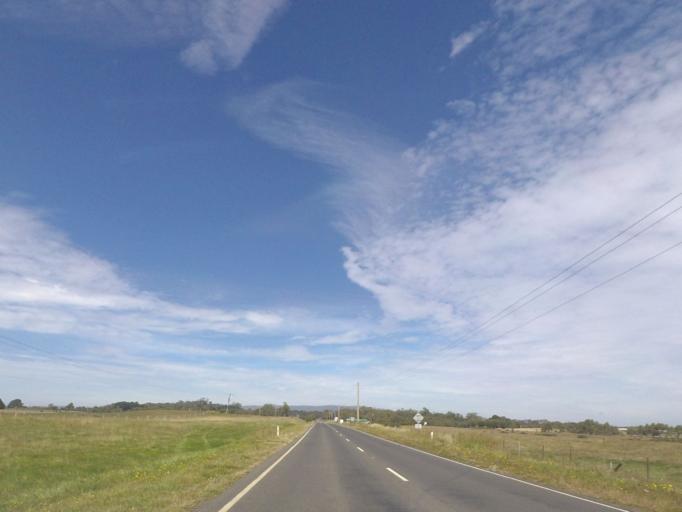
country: AU
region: Victoria
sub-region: Mount Alexander
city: Castlemaine
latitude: -37.2880
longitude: 144.5028
